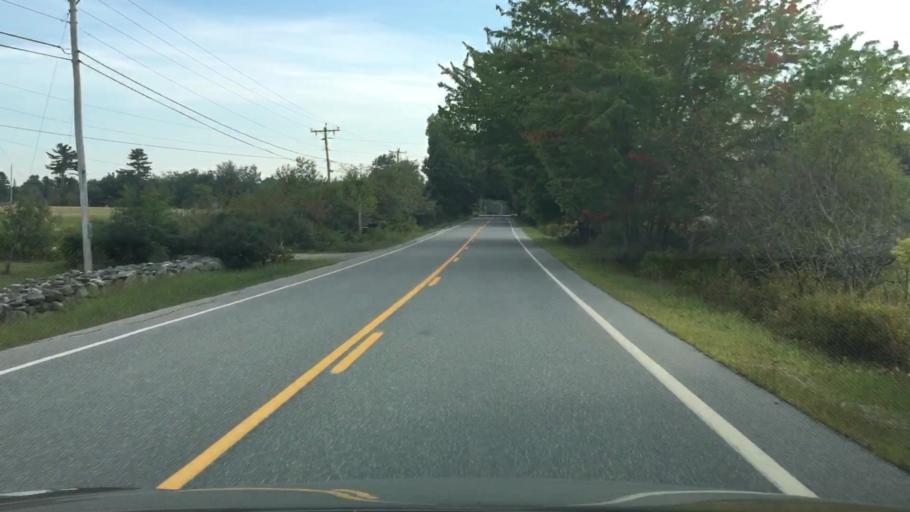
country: US
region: Maine
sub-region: Hancock County
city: Castine
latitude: 44.4401
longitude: -68.7897
